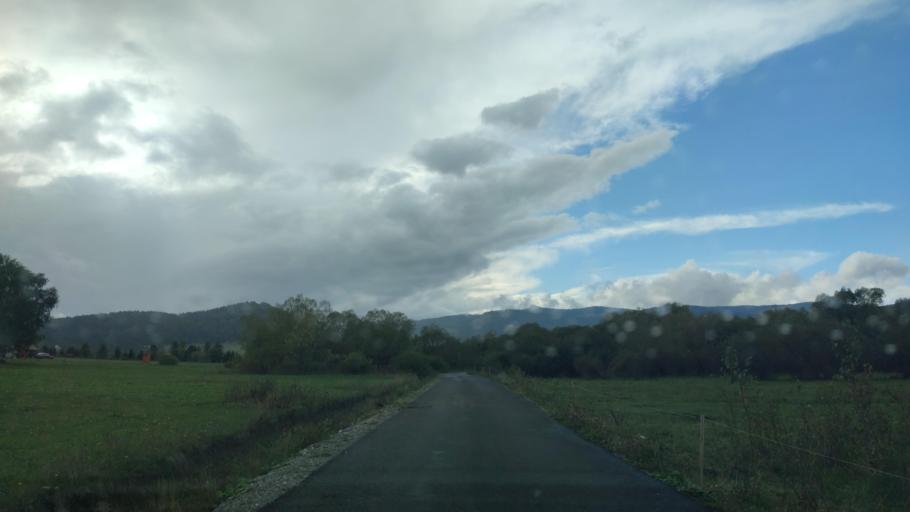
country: RO
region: Harghita
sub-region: Comuna Remetea
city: Remetea
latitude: 46.8137
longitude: 25.3891
